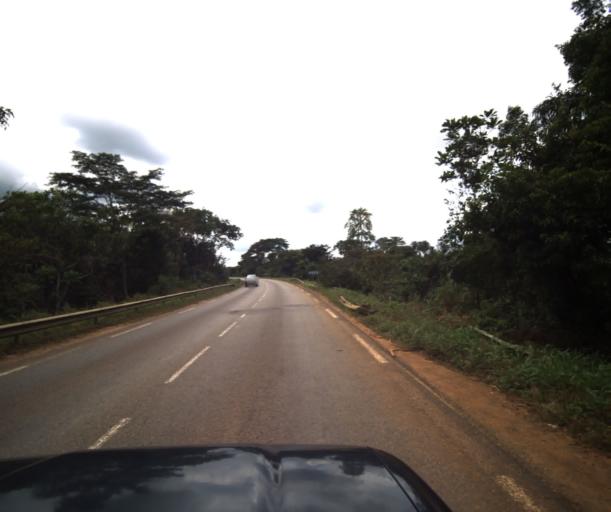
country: CM
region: Littoral
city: Edea
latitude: 3.8474
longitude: 10.4784
